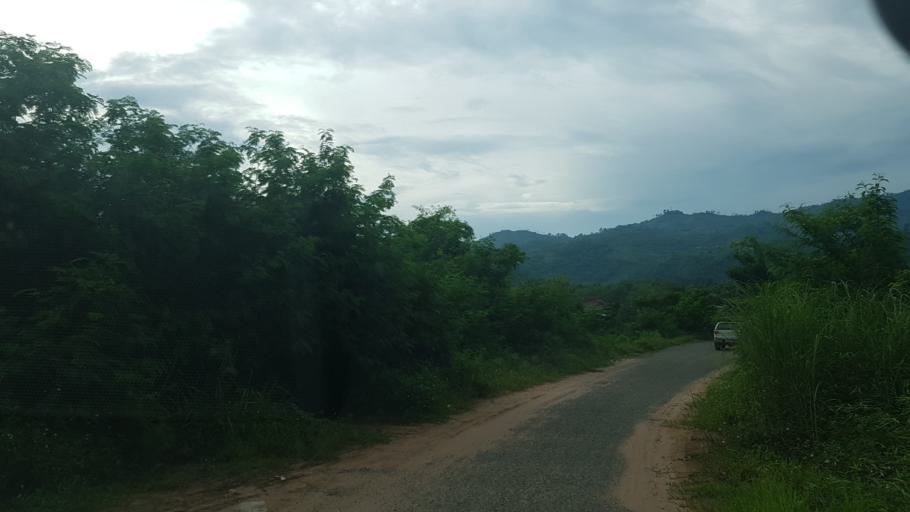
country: LA
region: Oudomxai
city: Muang Xay
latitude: 20.6949
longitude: 101.9900
